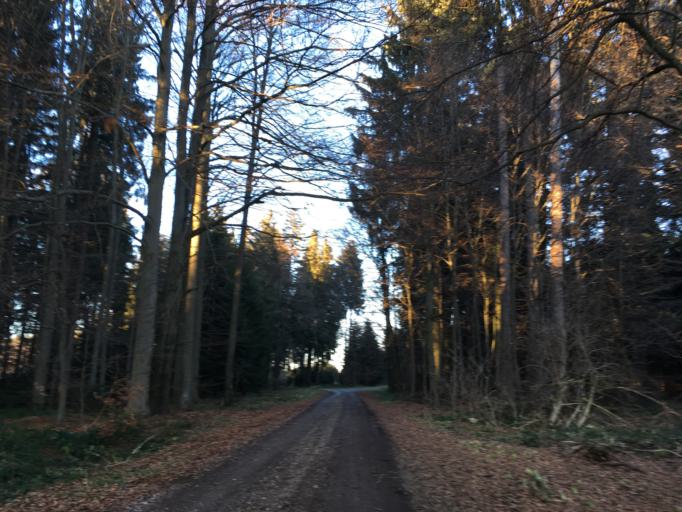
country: DE
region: Bavaria
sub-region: Swabia
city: Bohen
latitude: 47.8667
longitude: 10.2868
